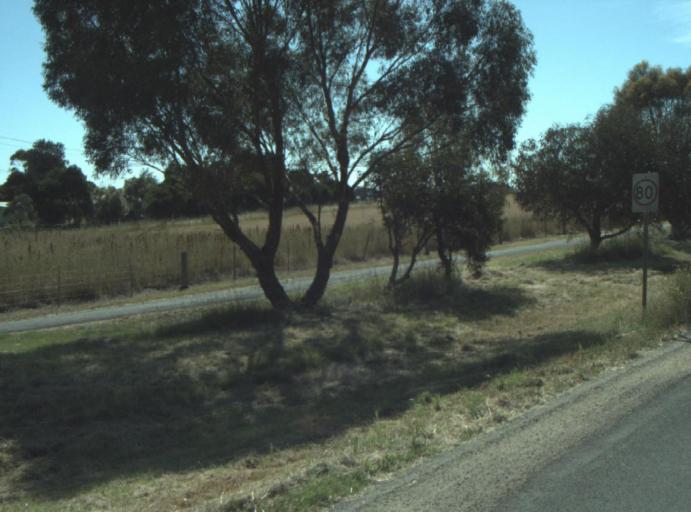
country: AU
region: Victoria
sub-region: Greater Geelong
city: Bell Post Hill
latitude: -38.0976
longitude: 144.3056
